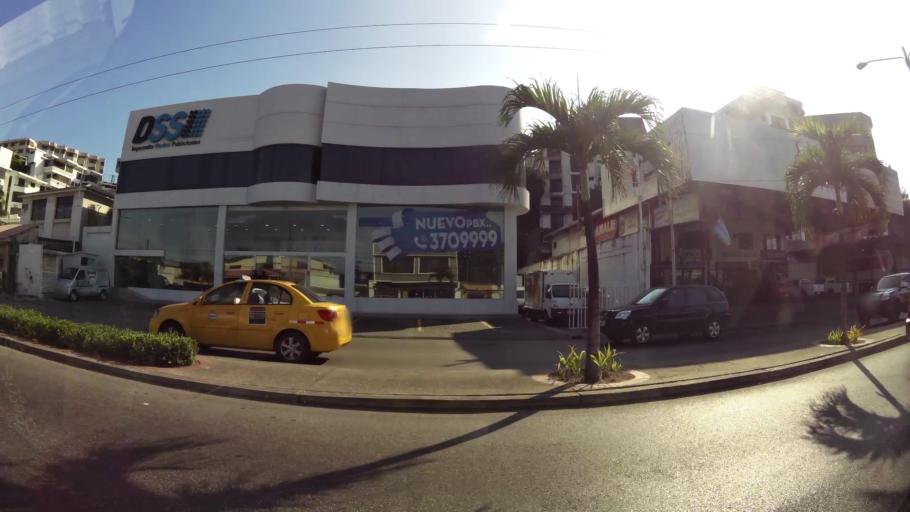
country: EC
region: Guayas
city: Guayaquil
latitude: -2.1671
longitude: -79.9042
